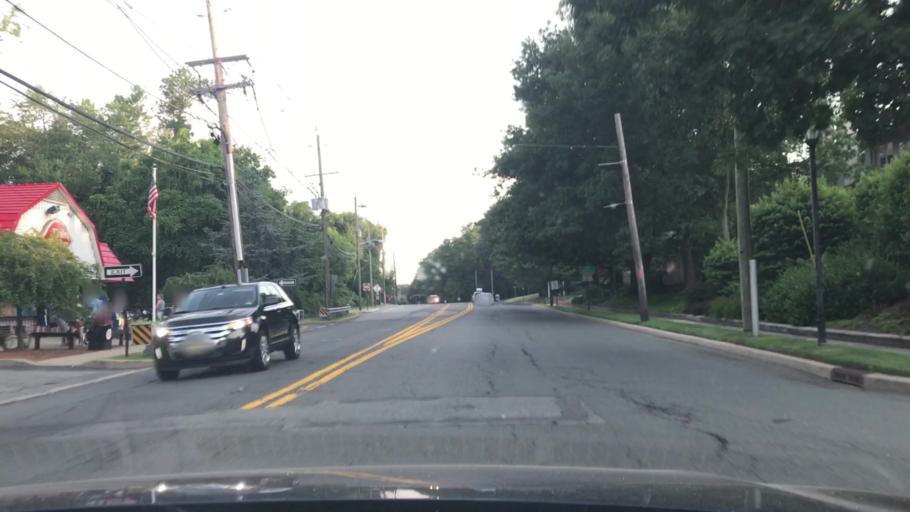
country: US
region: New Jersey
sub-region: Bergen County
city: Emerson
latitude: 40.9707
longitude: -74.0294
